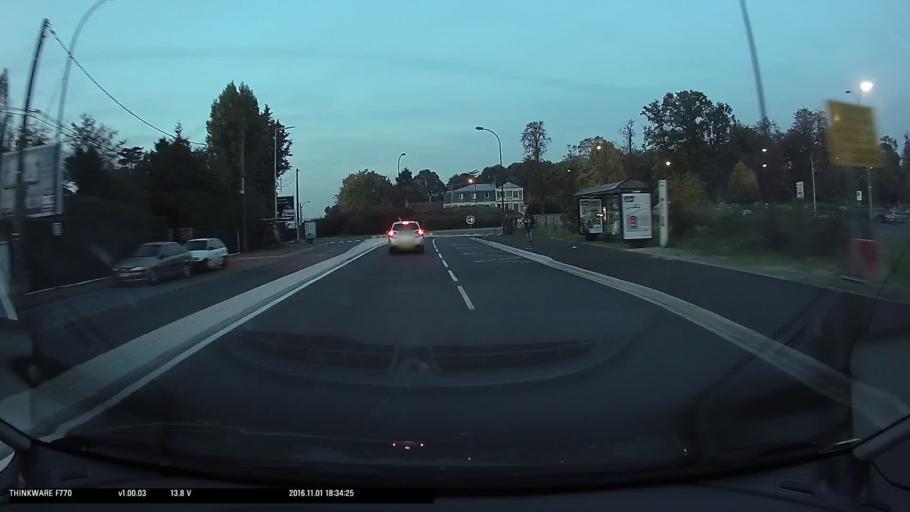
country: FR
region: Ile-de-France
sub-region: Departement de l'Essonne
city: Villemoisson-sur-Orge
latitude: 48.6612
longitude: 2.3407
